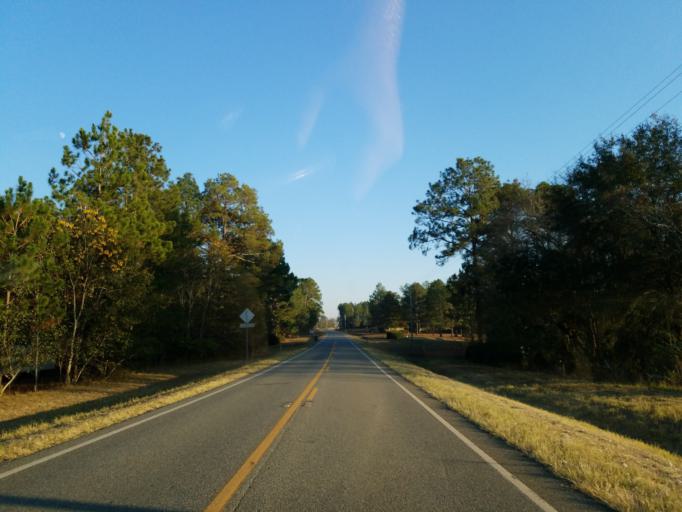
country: US
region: Georgia
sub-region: Crisp County
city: Cordele
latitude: 31.8782
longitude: -83.6723
